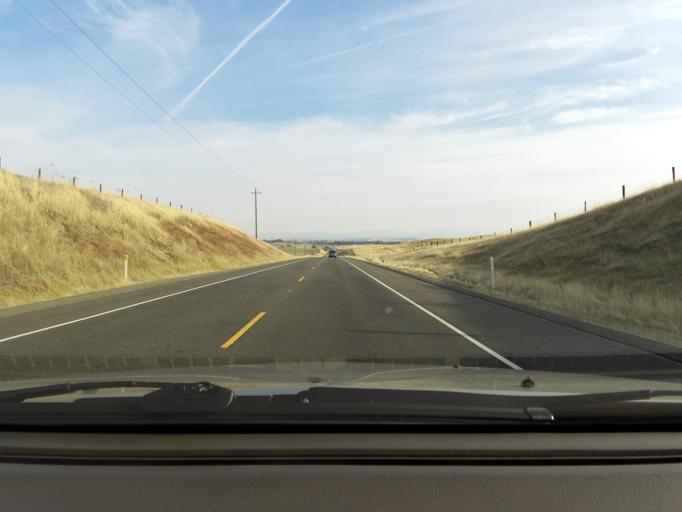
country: US
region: California
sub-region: Madera County
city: Bonadelle Ranchos-Madera Ranchos
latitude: 37.0301
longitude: -119.7875
